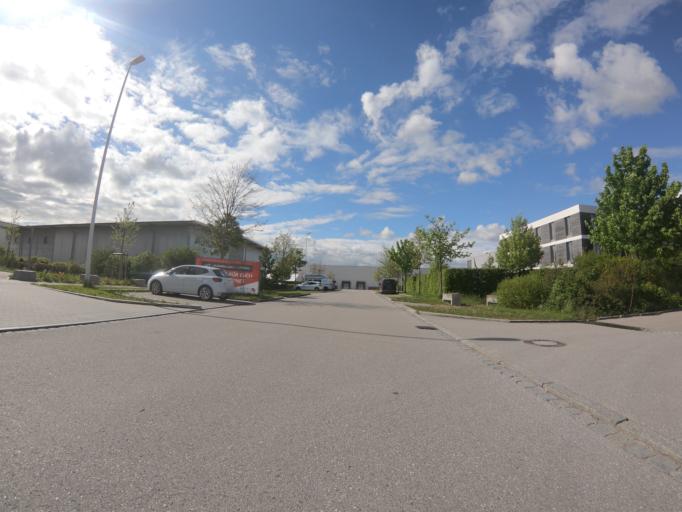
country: DE
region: Bavaria
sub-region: Upper Bavaria
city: Gilching
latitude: 48.0940
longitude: 11.3121
